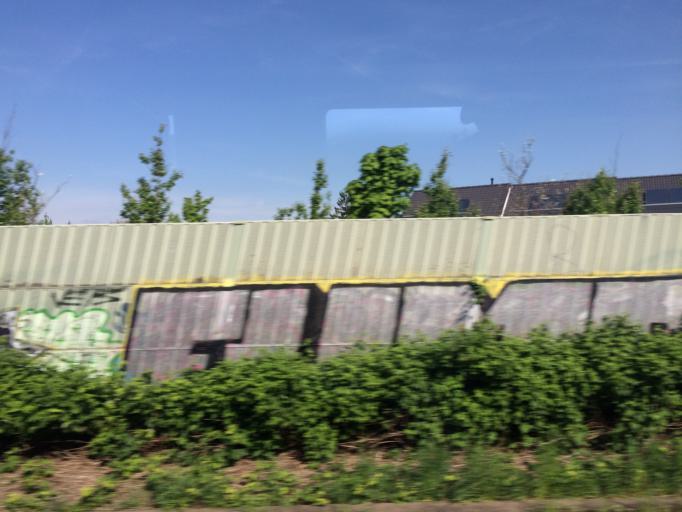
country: DE
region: North Rhine-Westphalia
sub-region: Regierungsbezirk Dusseldorf
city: Hochfeld
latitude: 51.3498
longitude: 6.7794
